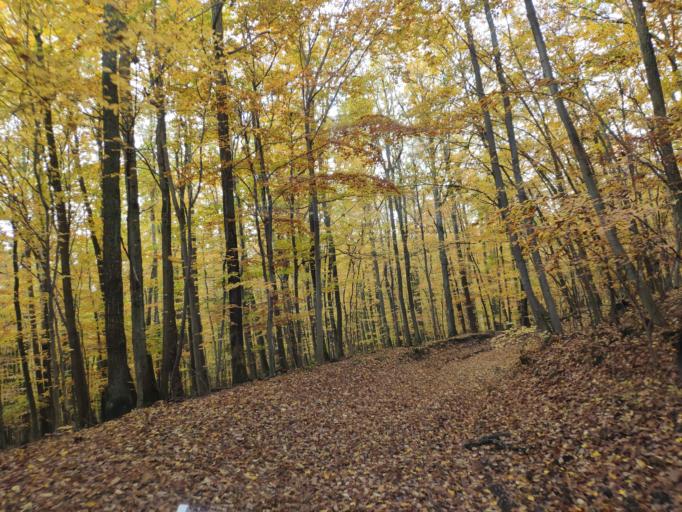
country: SK
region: Kosicky
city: Moldava nad Bodvou
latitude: 48.7189
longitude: 21.0120
